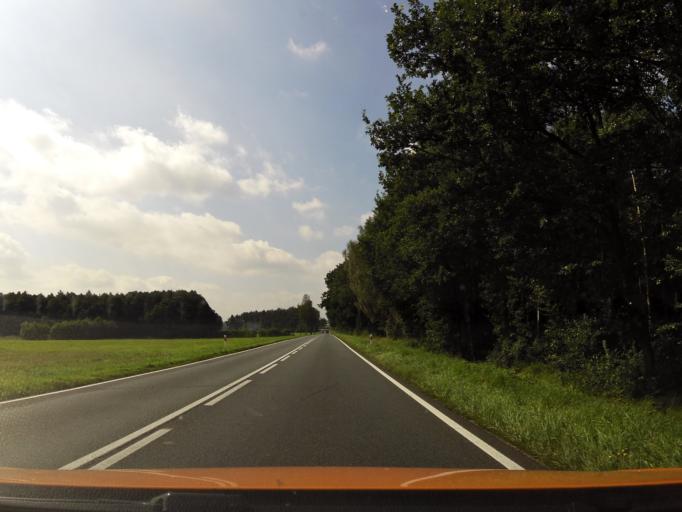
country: PL
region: West Pomeranian Voivodeship
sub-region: Powiat gryficki
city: Ploty
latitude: 53.7613
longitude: 15.2318
